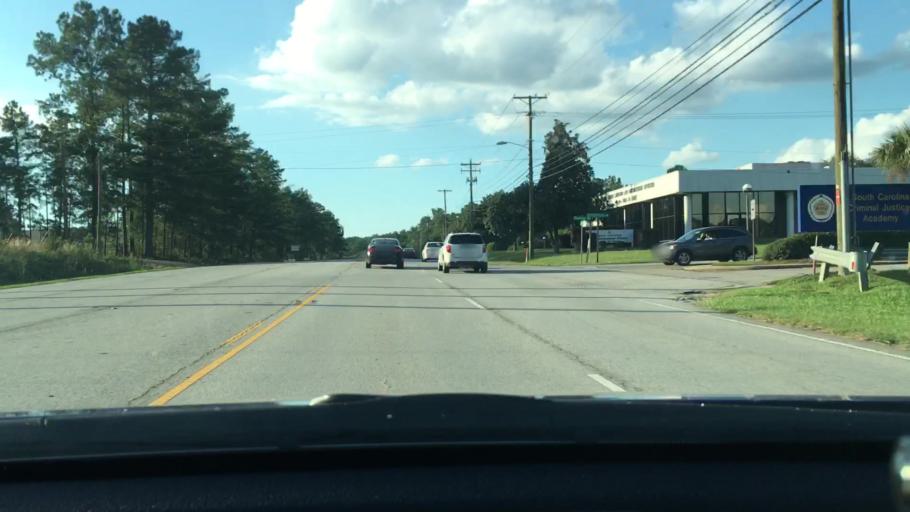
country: US
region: South Carolina
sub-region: Lexington County
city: Saint Andrews
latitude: 34.0758
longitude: -81.1256
